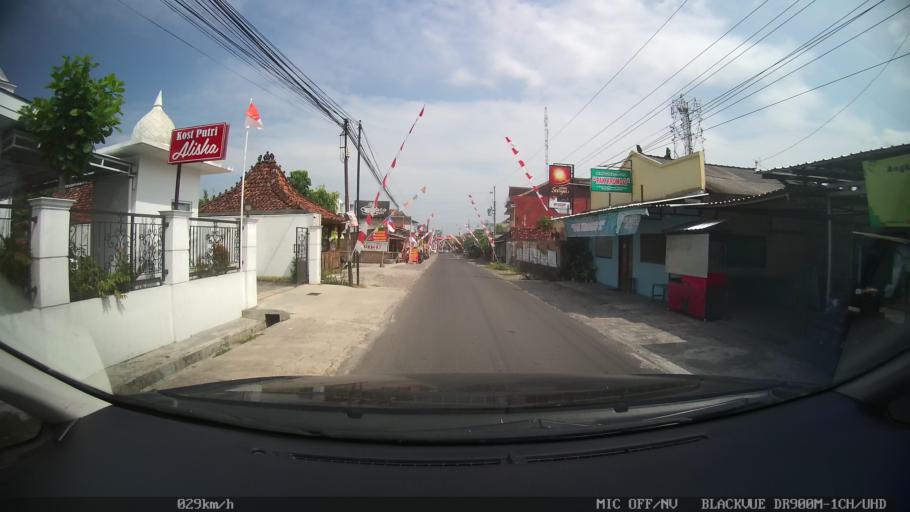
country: ID
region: Daerah Istimewa Yogyakarta
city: Depok
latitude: -7.7621
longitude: 110.4224
